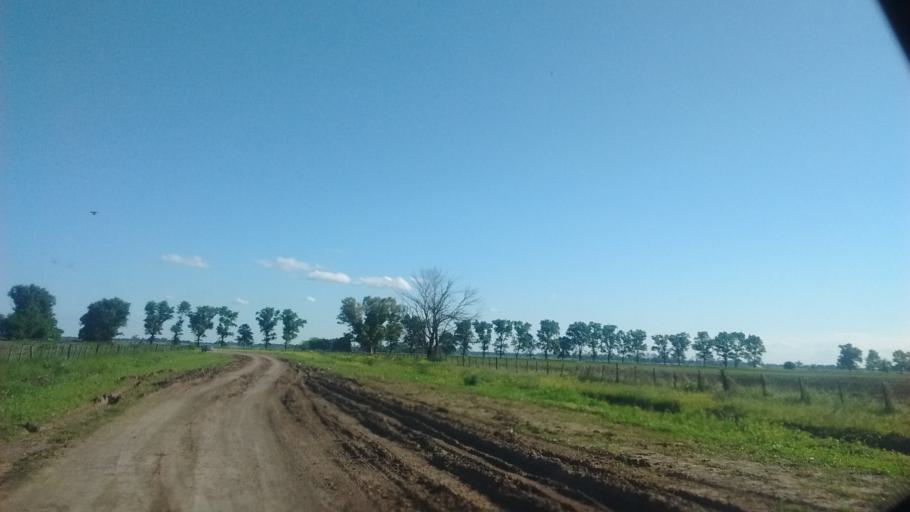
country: AR
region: Santa Fe
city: Funes
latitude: -32.8702
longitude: -60.7987
